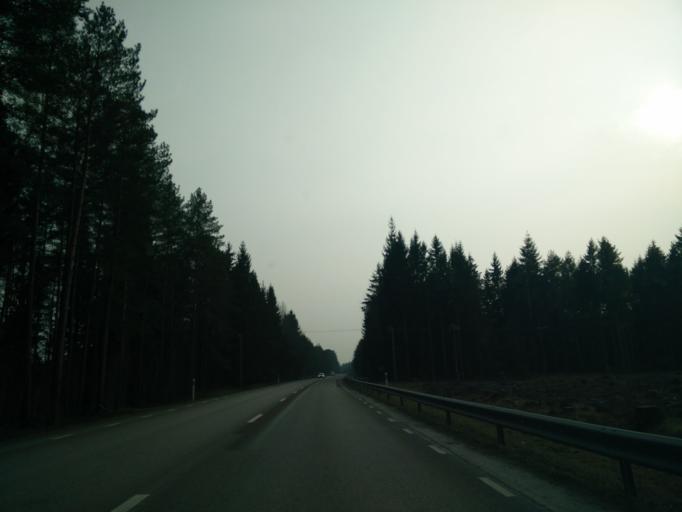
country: SE
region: Vaermland
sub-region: Forshaga Kommun
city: Forshaga
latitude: 59.4907
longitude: 13.4238
